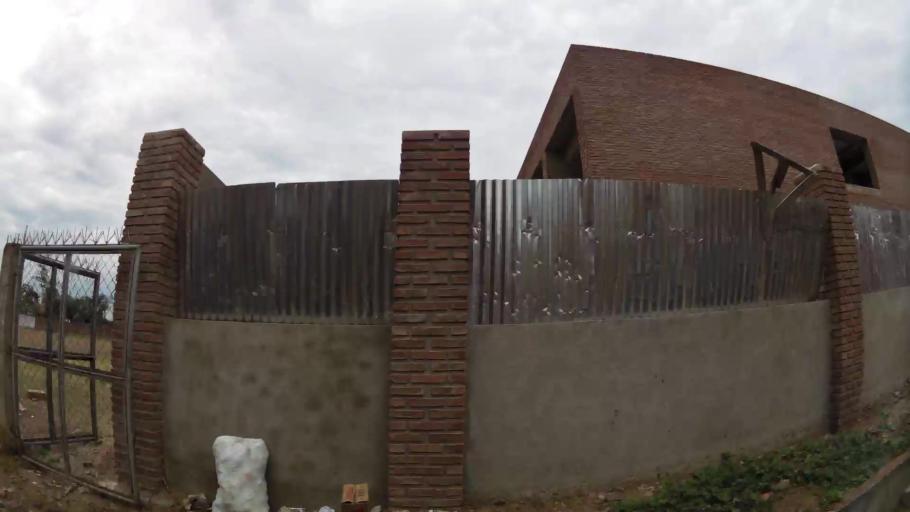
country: BO
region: Santa Cruz
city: Santa Cruz de la Sierra
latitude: -17.7567
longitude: -63.1614
